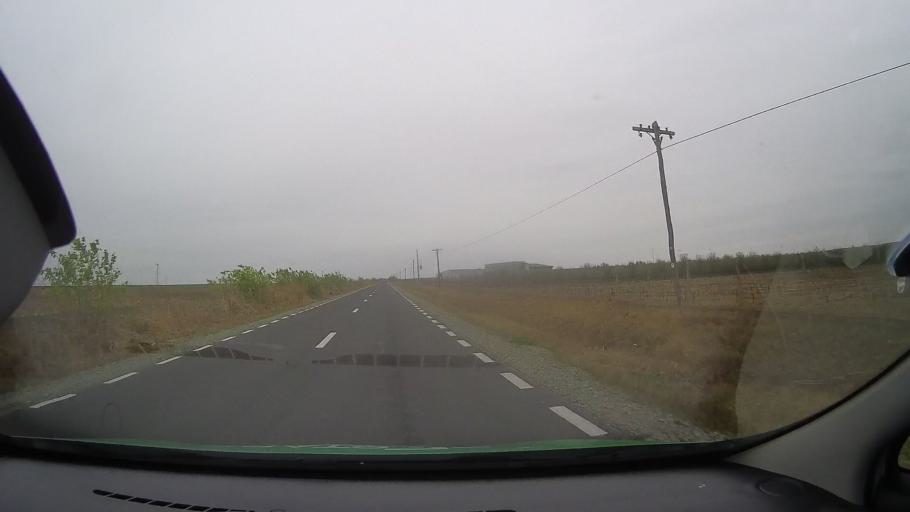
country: RO
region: Constanta
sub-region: Comuna Tortoman
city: Tortoman
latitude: 44.3658
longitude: 28.2085
